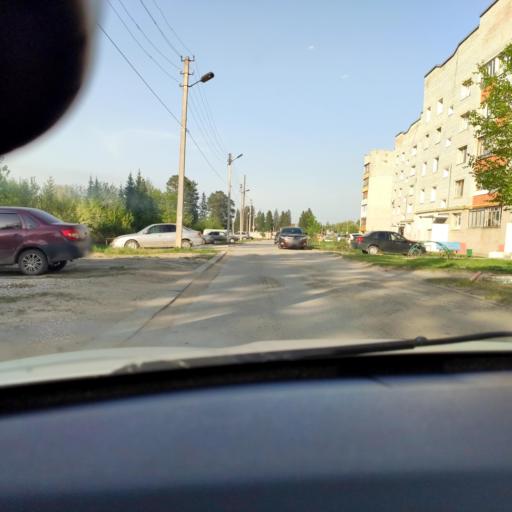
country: RU
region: Perm
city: Polazna
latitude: 58.2970
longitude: 56.3880
